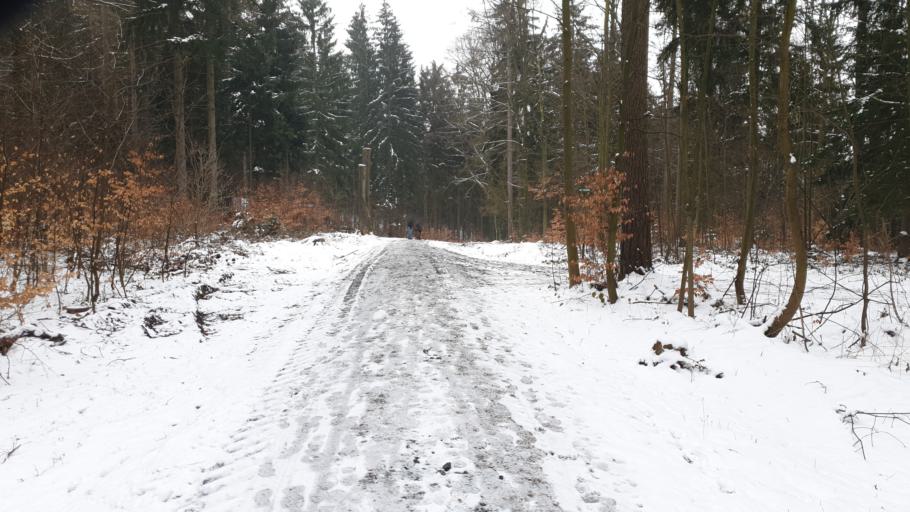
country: DE
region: Saxony
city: Gornau
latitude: 50.7713
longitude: 12.9909
